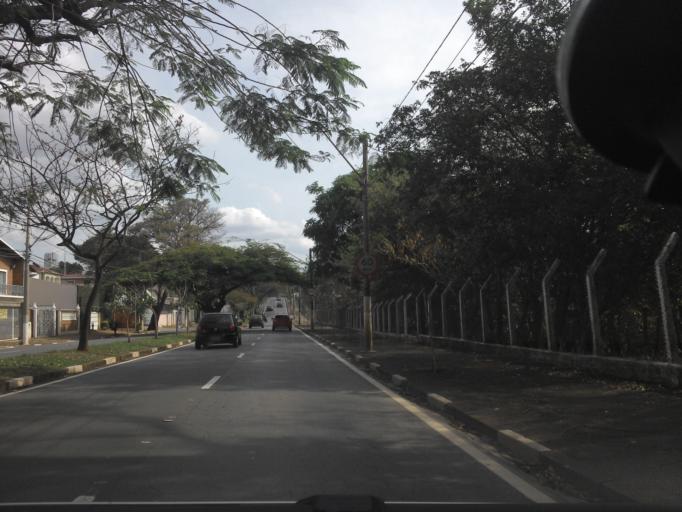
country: BR
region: Sao Paulo
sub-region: Campinas
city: Campinas
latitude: -22.8845
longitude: -47.0773
